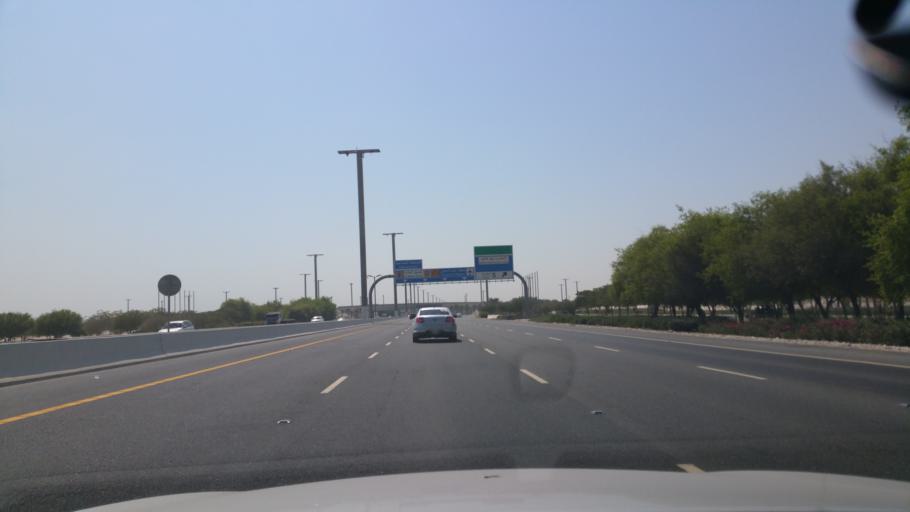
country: QA
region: Baladiyat ad Dawhah
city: Doha
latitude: 25.2655
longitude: 51.5804
